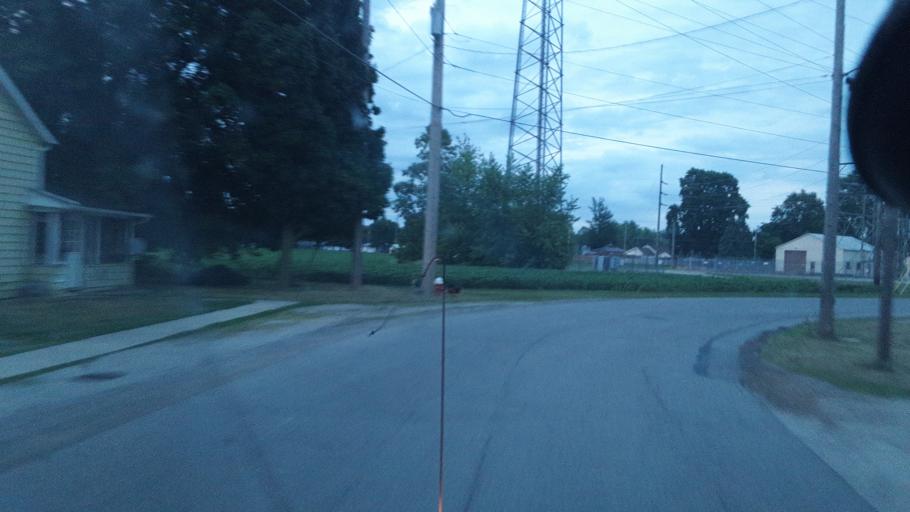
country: US
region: Ohio
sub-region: Defiance County
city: Hicksville
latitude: 41.2983
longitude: -84.7636
